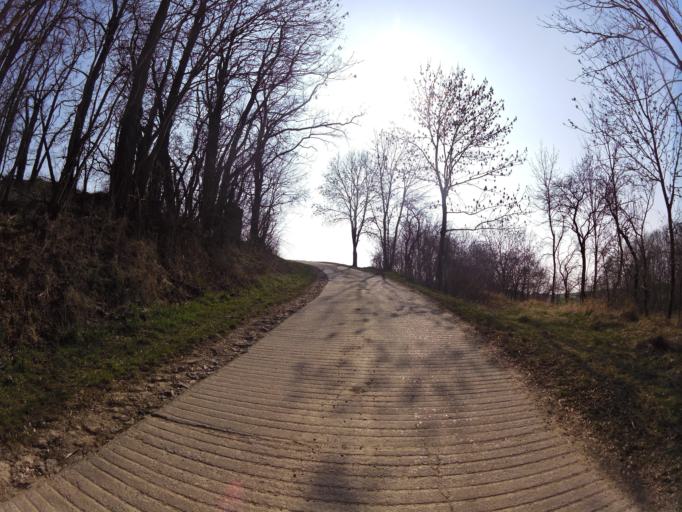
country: DE
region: Bavaria
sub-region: Regierungsbezirk Unterfranken
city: Gaukonigshofen
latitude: 49.6648
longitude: 9.9912
